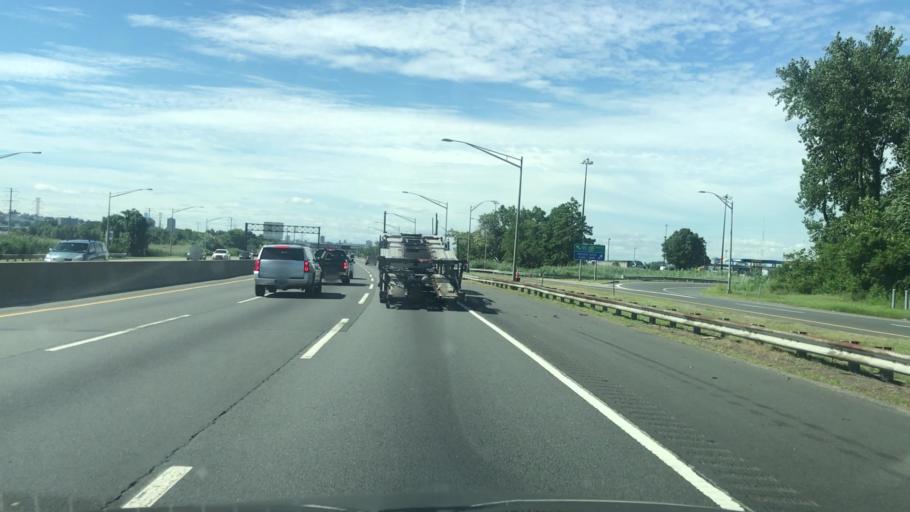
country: US
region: New Jersey
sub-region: Bergen County
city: Ridgefield
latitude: 40.8251
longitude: -74.0279
